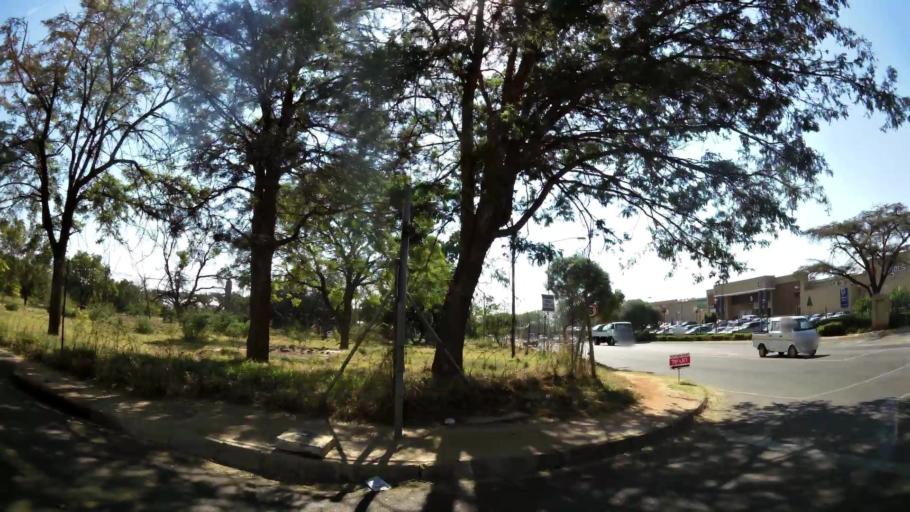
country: ZA
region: Gauteng
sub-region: City of Tshwane Metropolitan Municipality
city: Pretoria
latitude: -25.6821
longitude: 28.2477
